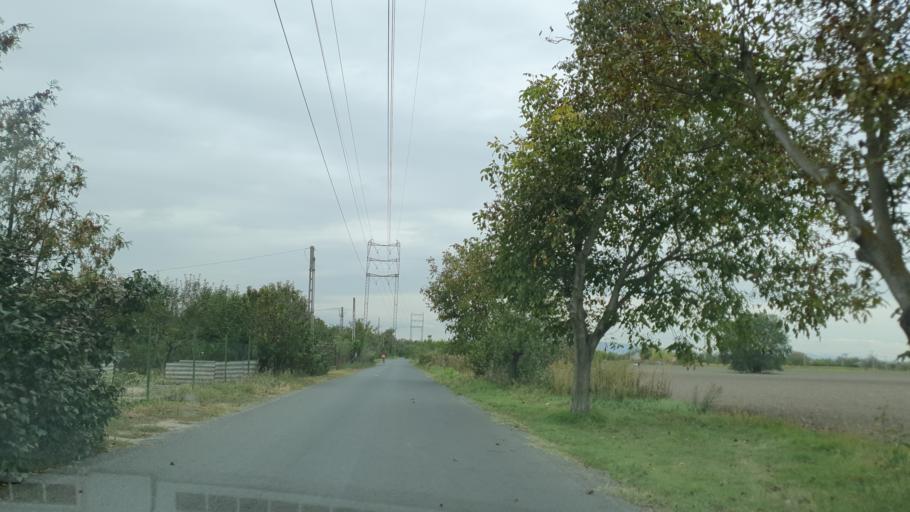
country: HU
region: Pest
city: Dunaharaszti
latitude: 47.3804
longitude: 19.0825
